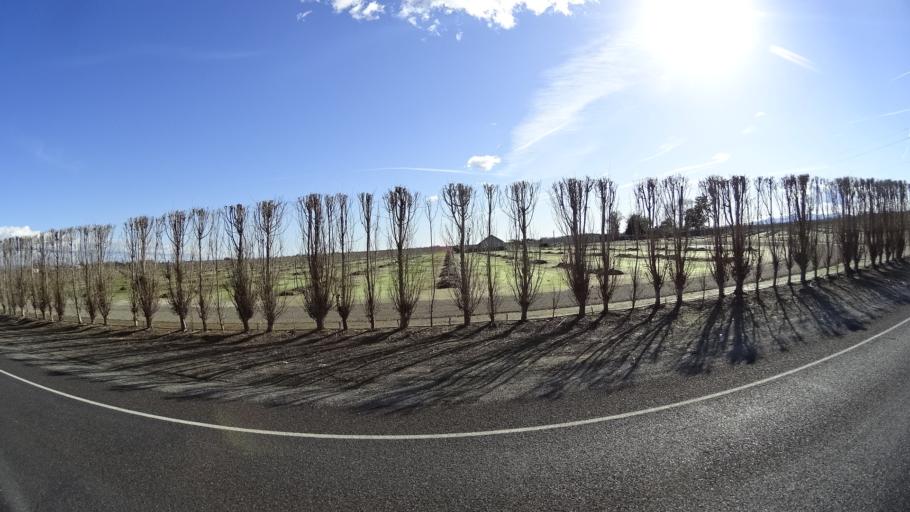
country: US
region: California
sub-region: Butte County
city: Gridley
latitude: 39.3644
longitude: -121.6167
